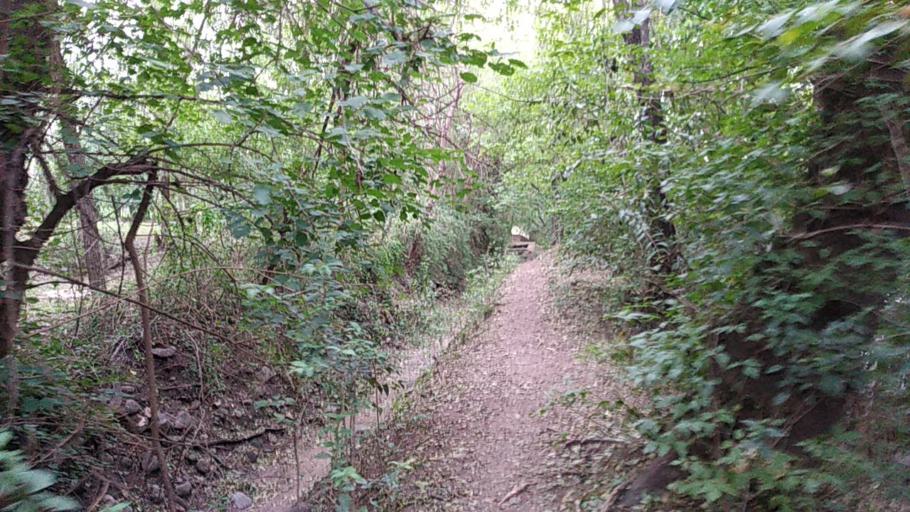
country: AR
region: Cordoba
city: Alta Gracia
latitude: -31.7249
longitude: -64.4351
